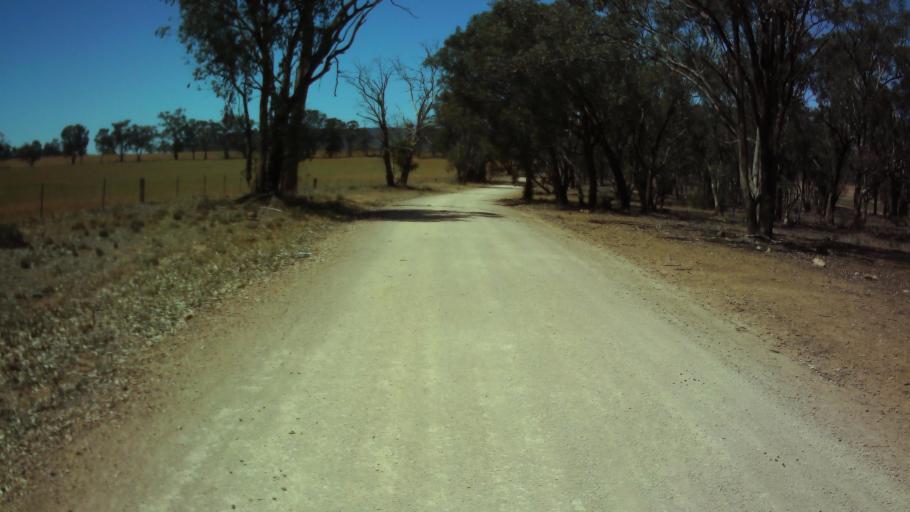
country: AU
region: New South Wales
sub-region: Weddin
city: Grenfell
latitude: -33.9284
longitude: 148.0780
